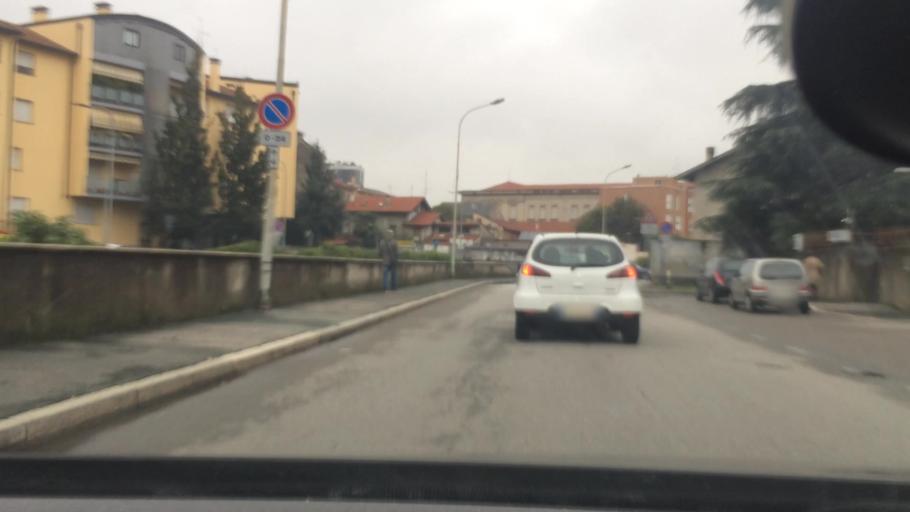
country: IT
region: Lombardy
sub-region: Citta metropolitana di Milano
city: Legnano
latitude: 45.5905
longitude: 8.9208
